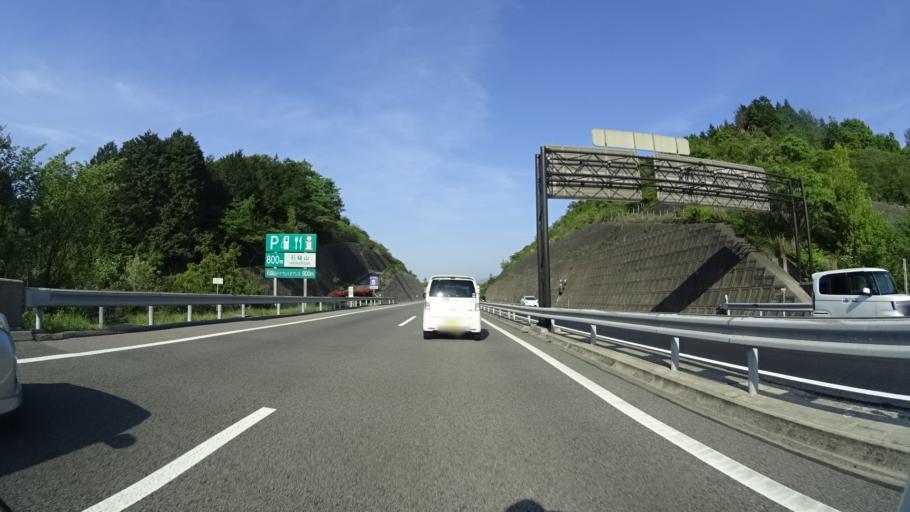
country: JP
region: Ehime
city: Saijo
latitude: 33.8851
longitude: 133.0983
